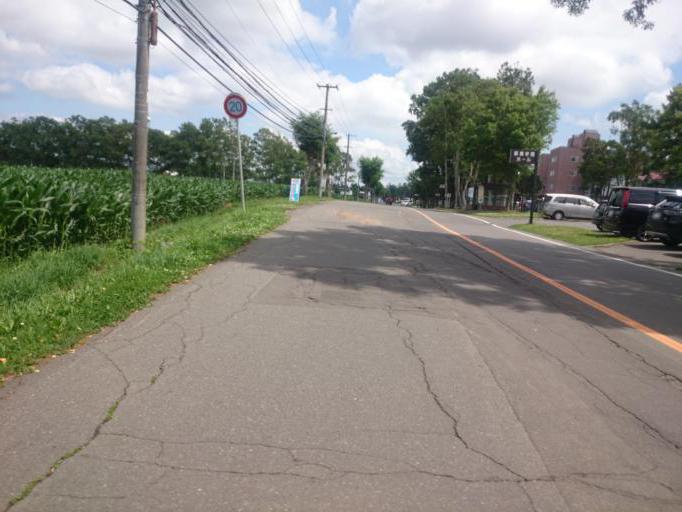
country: JP
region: Hokkaido
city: Ebetsu
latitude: 43.0735
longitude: 141.5079
